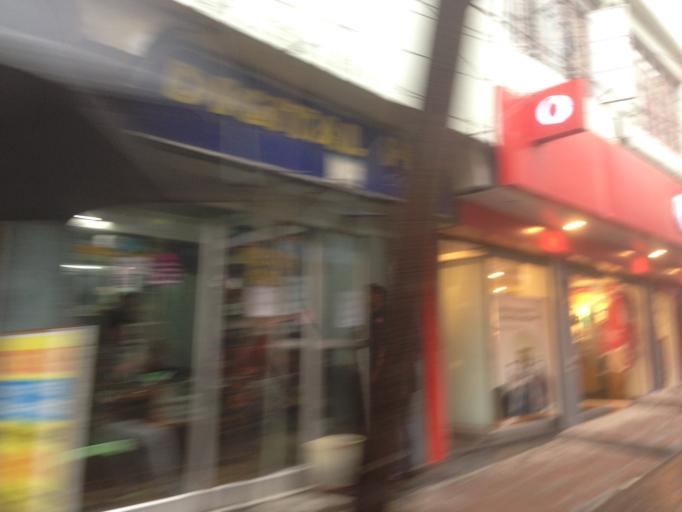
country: IN
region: West Bengal
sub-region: Darjiling
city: Darjiling
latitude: 27.0446
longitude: 88.2668
